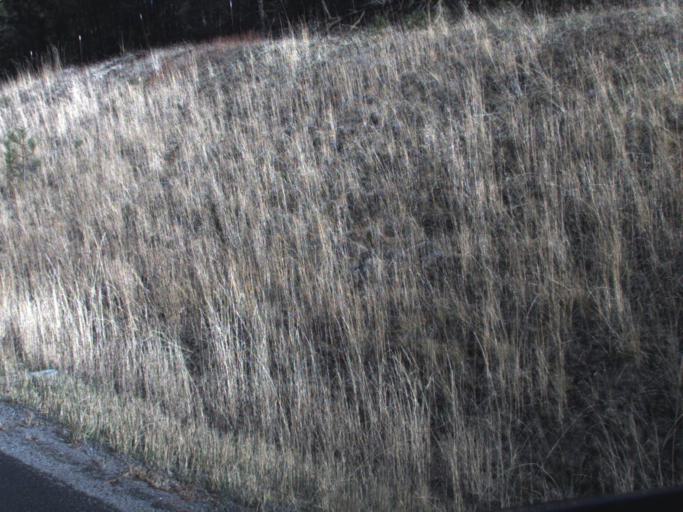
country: US
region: Washington
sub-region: Lincoln County
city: Davenport
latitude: 48.0388
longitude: -118.2282
